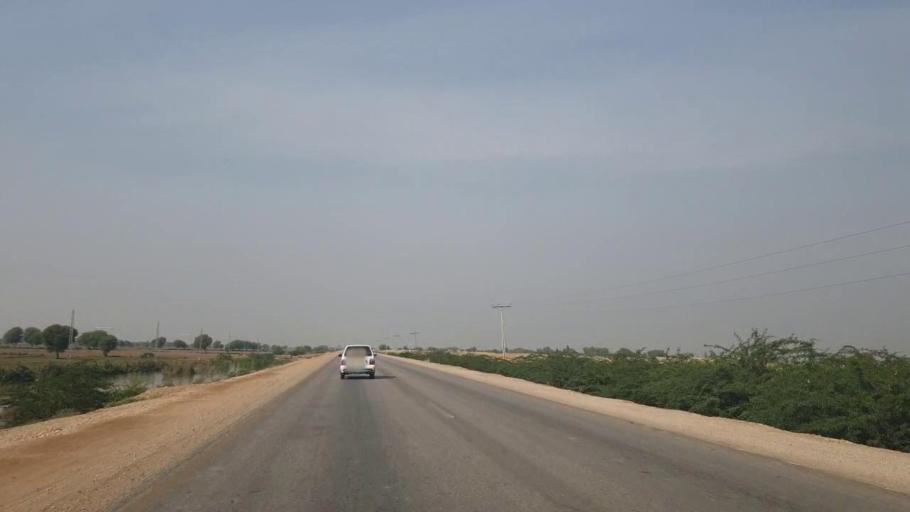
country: PK
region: Sindh
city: Sann
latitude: 26.0642
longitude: 68.1021
